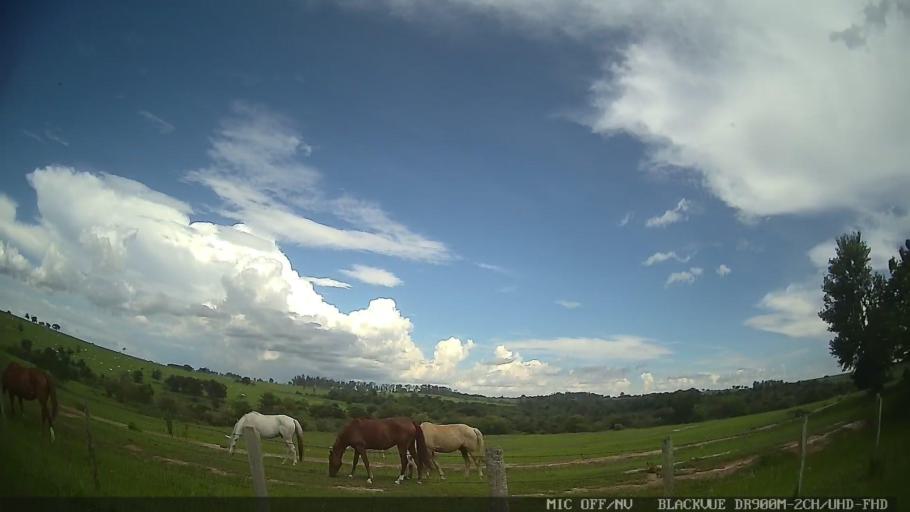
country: BR
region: Sao Paulo
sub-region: Conchas
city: Conchas
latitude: -22.9795
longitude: -47.9889
